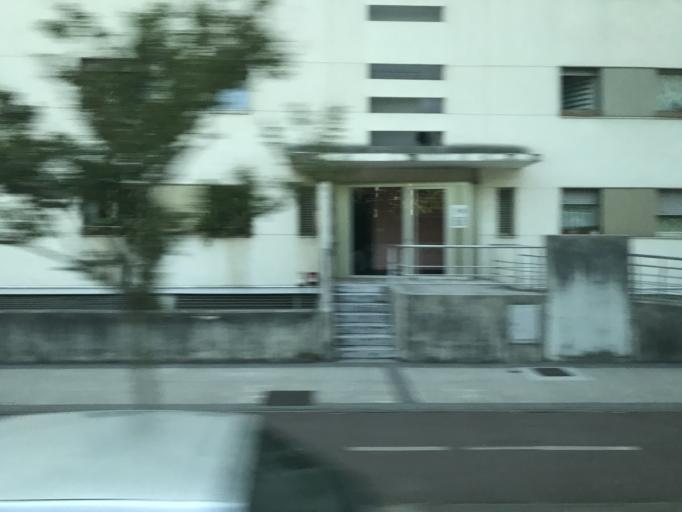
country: ES
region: Basque Country
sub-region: Provincia de Guipuzcoa
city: San Sebastian
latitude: 43.3135
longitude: -1.9777
